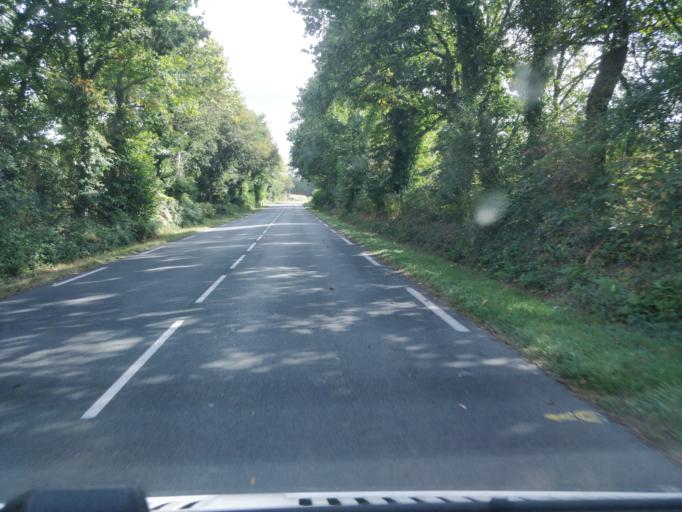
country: FR
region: Brittany
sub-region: Departement du Finistere
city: Landudec
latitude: 47.9994
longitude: -4.3021
